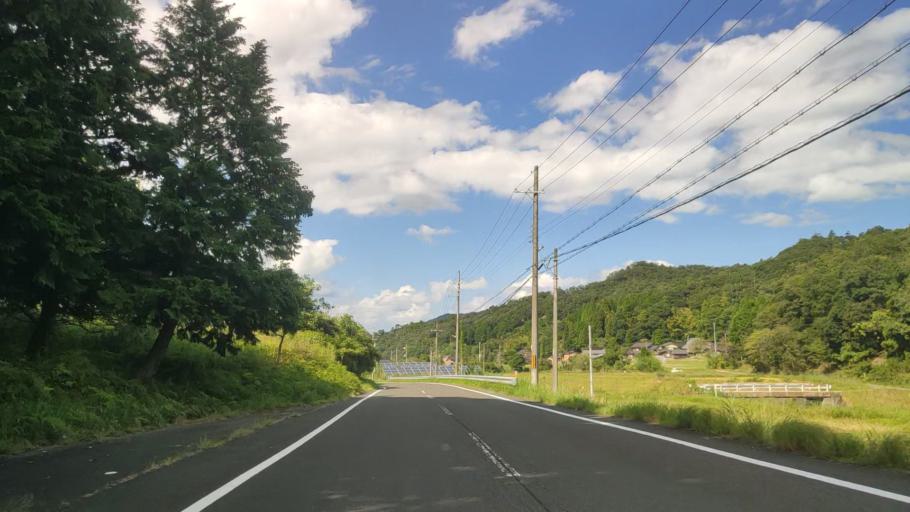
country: JP
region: Hyogo
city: Toyooka
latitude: 35.5591
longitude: 134.9795
